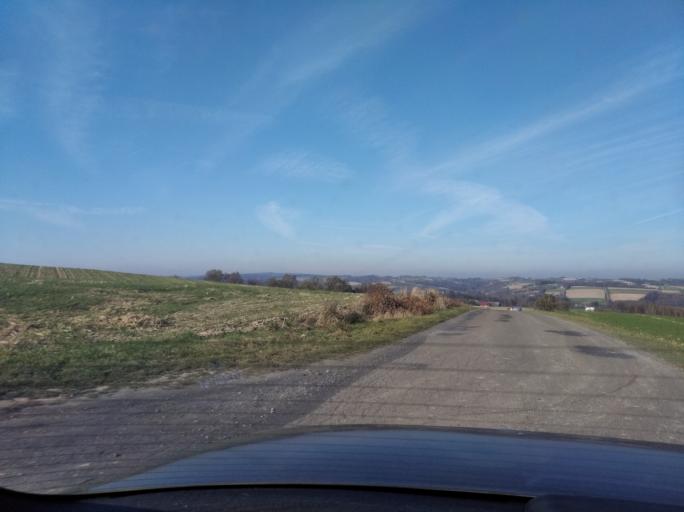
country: PL
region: Subcarpathian Voivodeship
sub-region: Powiat ropczycko-sedziszowski
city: Wielopole Skrzynskie
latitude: 49.9165
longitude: 21.5659
